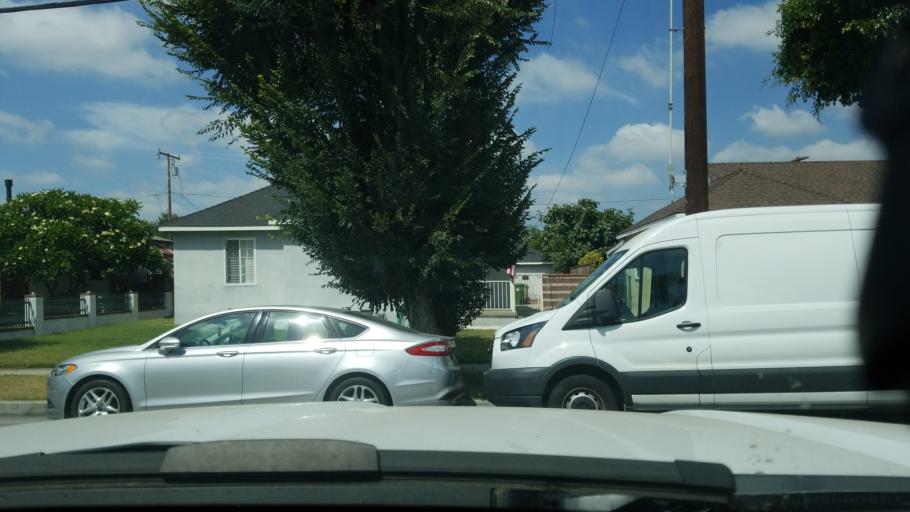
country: US
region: California
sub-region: Los Angeles County
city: West Whittier-Los Nietos
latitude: 33.9770
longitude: -118.0654
